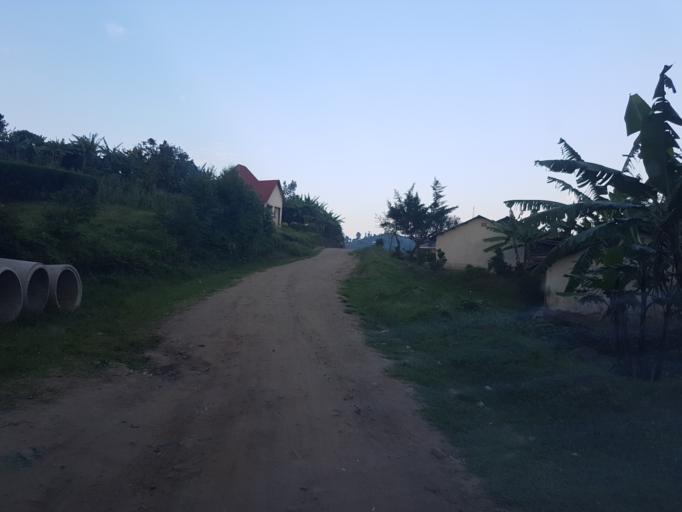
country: UG
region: Western Region
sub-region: Mitoma District
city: Mitoma
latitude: -0.6779
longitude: 29.9226
